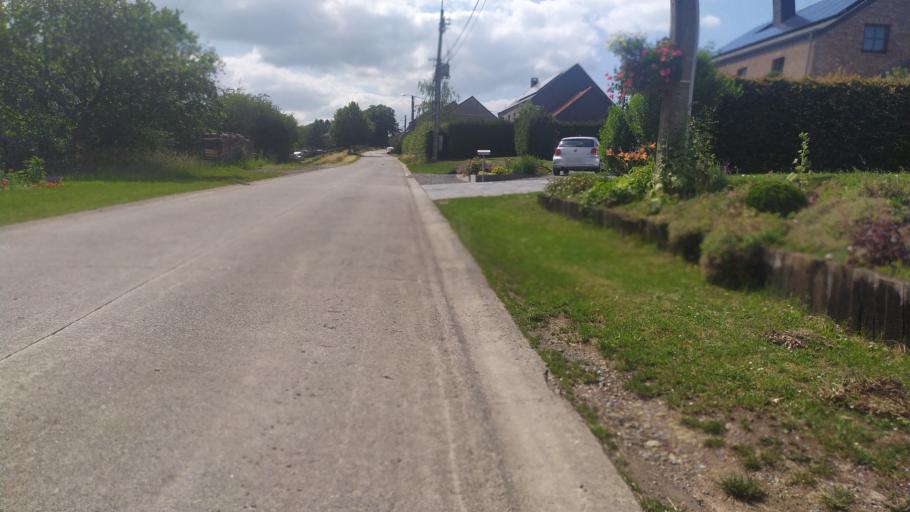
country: BE
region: Wallonia
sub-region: Province du Luxembourg
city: Wellin
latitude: 50.0679
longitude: 5.0768
